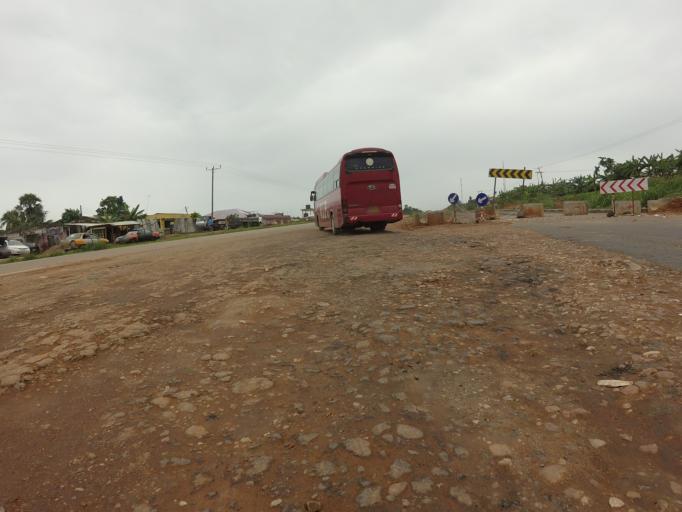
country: GH
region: Eastern
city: Suhum
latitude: 6.0425
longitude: -0.4584
